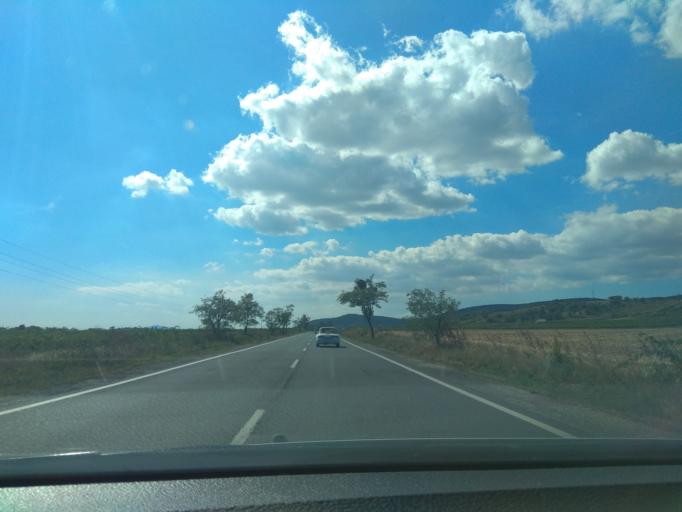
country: HU
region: Borsod-Abauj-Zemplen
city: Sarospatak
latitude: 48.3136
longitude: 21.5331
